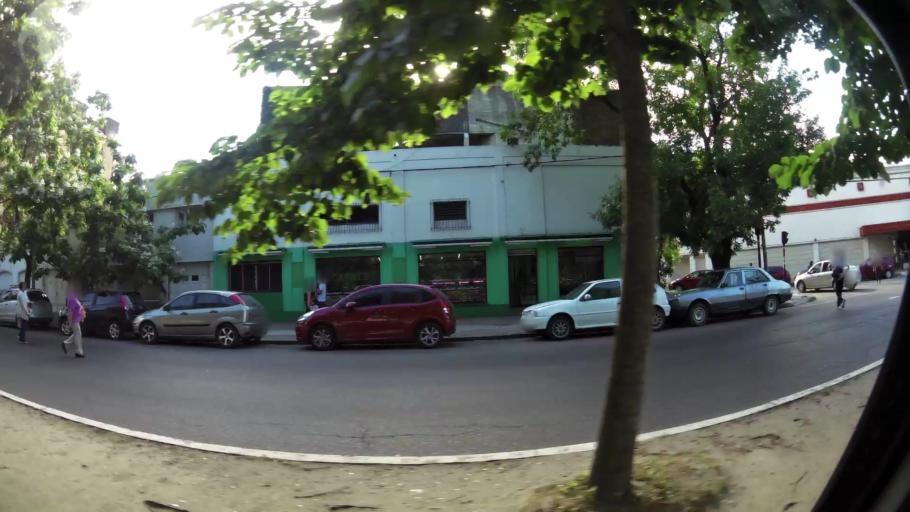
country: AR
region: Buenos Aires
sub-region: Partido de La Plata
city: La Plata
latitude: -34.9018
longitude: -57.9493
